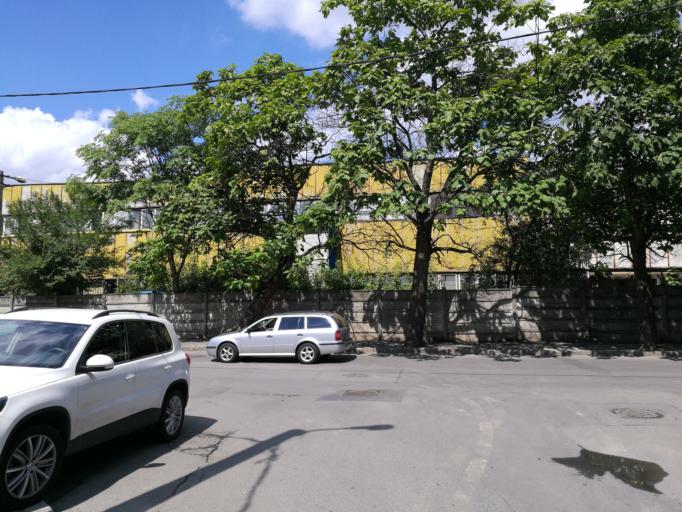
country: RO
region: Bucuresti
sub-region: Municipiul Bucuresti
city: Bucharest
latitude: 44.4916
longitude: 26.0914
